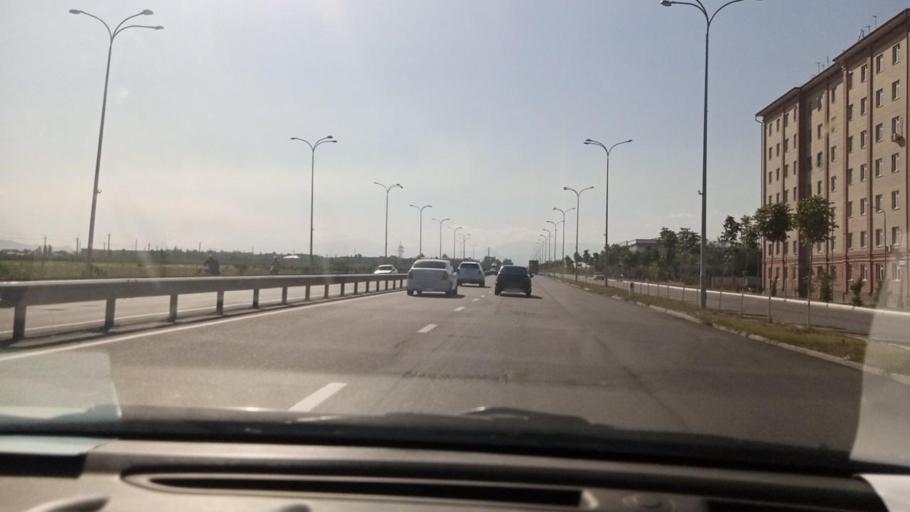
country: UZ
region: Toshkent
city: Ohangaron
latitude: 40.9138
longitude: 69.6106
